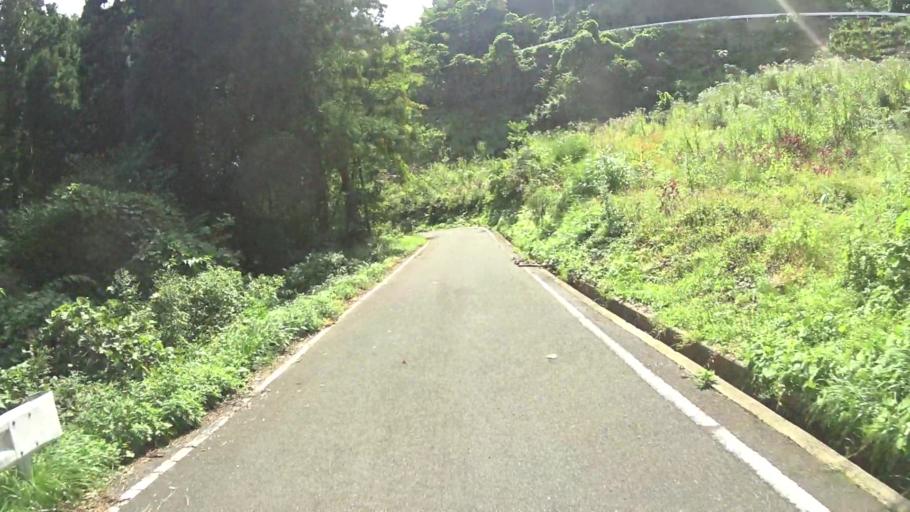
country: JP
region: Kyoto
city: Miyazu
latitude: 35.6619
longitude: 135.2315
